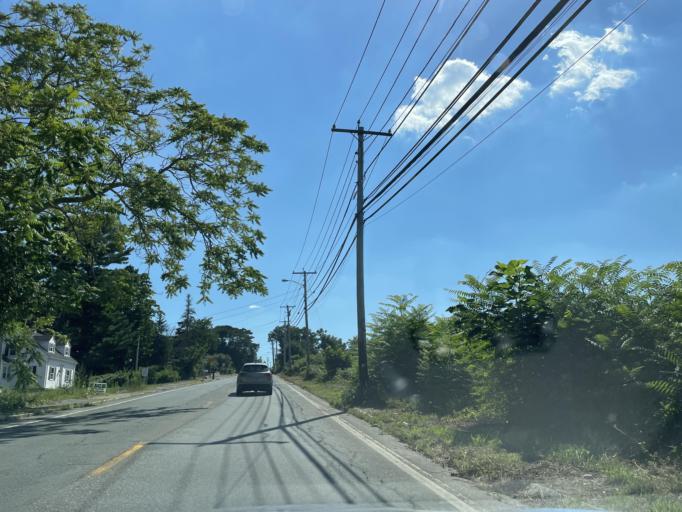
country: US
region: Massachusetts
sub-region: Worcester County
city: Mendon
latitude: 42.1100
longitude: -71.5513
